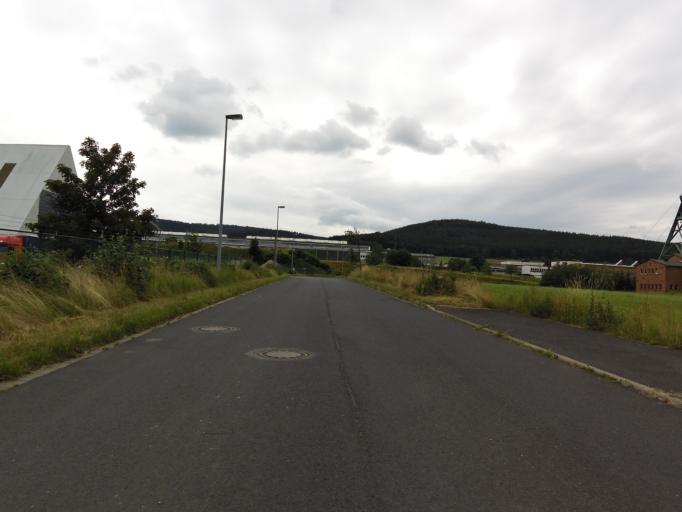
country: DE
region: Thuringia
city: Stadtlengsfeld
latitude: 50.8210
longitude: 10.1255
